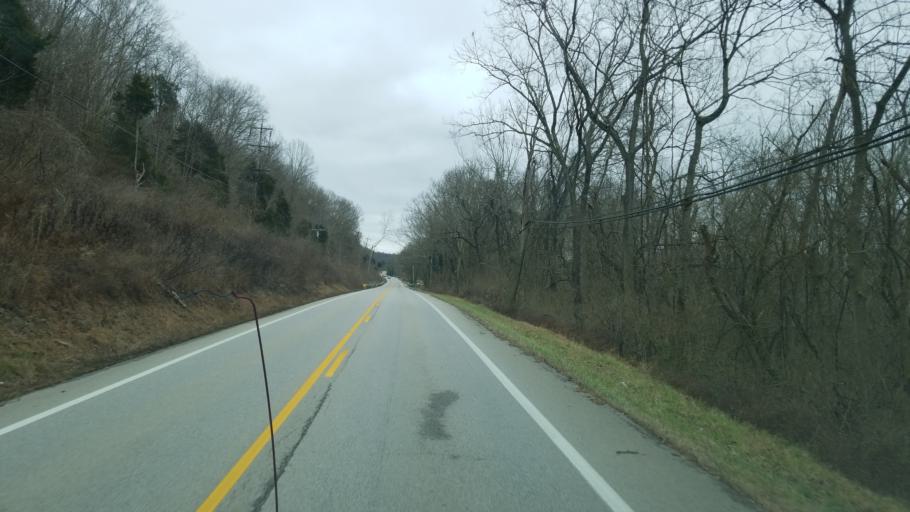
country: US
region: Ohio
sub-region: Clermont County
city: New Richmond
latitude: 38.9094
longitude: -84.2458
